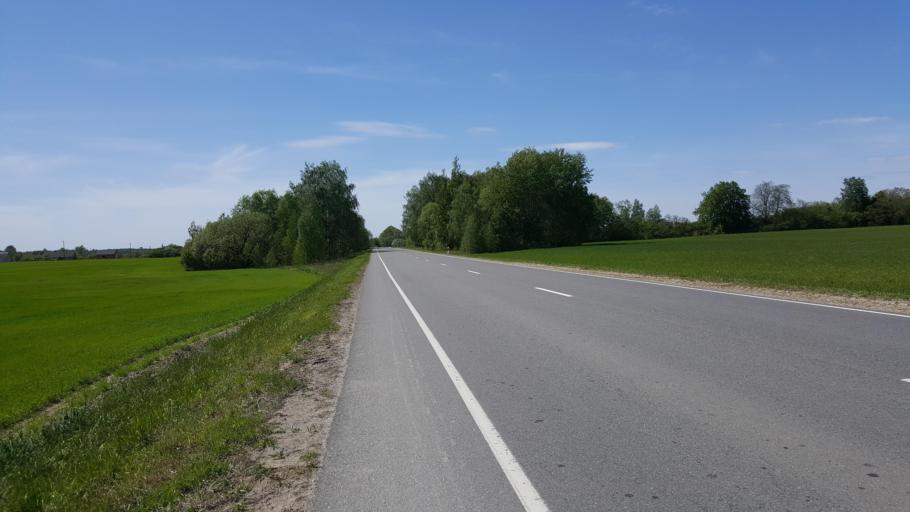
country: BY
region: Brest
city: Zhabinka
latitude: 52.3585
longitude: 24.1633
